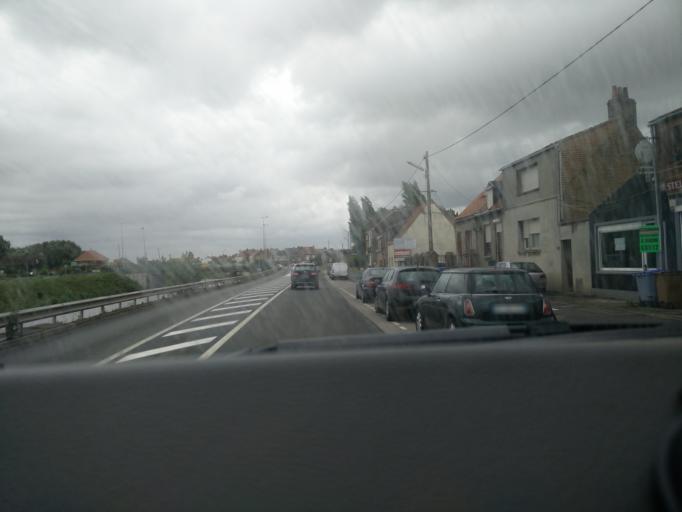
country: FR
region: Nord-Pas-de-Calais
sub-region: Departement du Nord
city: Coudekerque-Branche
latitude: 51.0039
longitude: 2.3828
